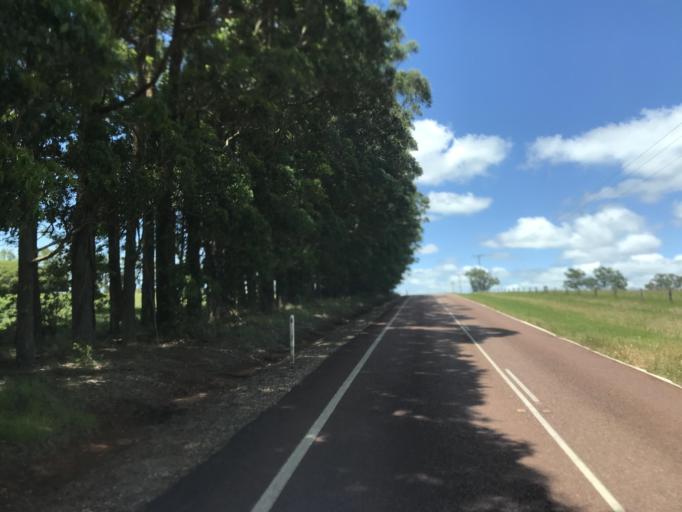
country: AU
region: Queensland
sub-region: Tablelands
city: Ravenshoe
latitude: -17.5308
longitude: 145.4535
